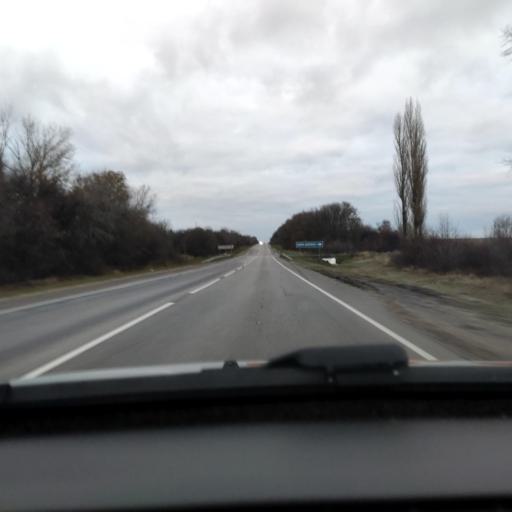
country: RU
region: Lipetsk
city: Khlevnoye
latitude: 52.3212
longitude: 39.1683
